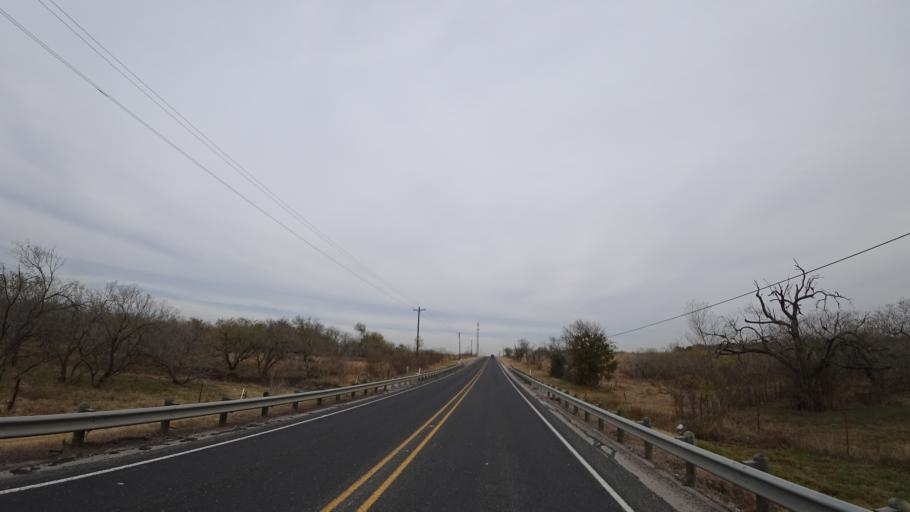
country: US
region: Texas
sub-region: Travis County
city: Onion Creek
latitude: 30.1308
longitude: -97.7091
